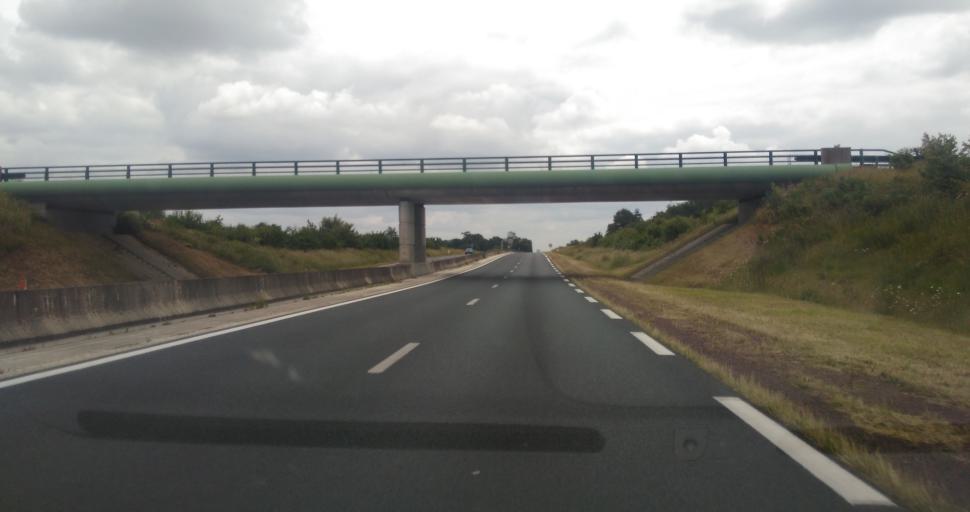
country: FR
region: Pays de la Loire
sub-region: Departement de la Vendee
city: Bournezeau
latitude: 46.6447
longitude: -1.2027
